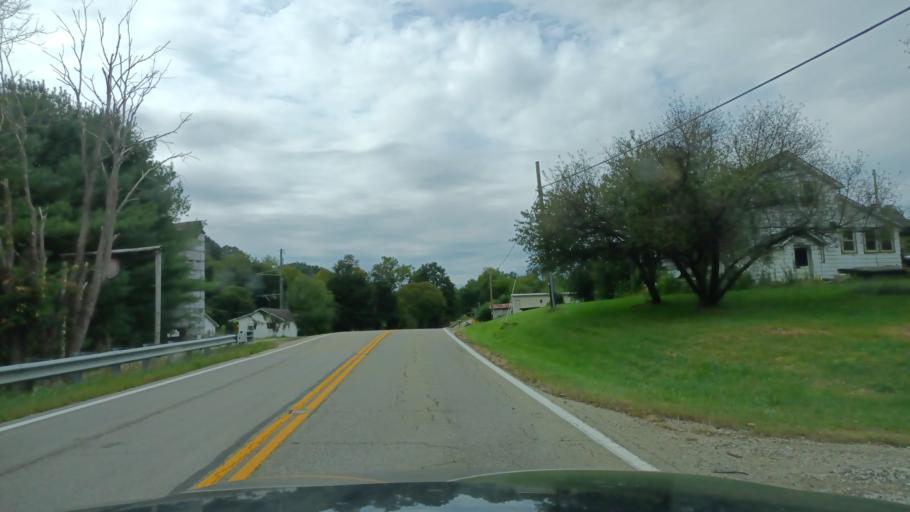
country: US
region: Ohio
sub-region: Vinton County
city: McArthur
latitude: 39.2725
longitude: -82.5211
